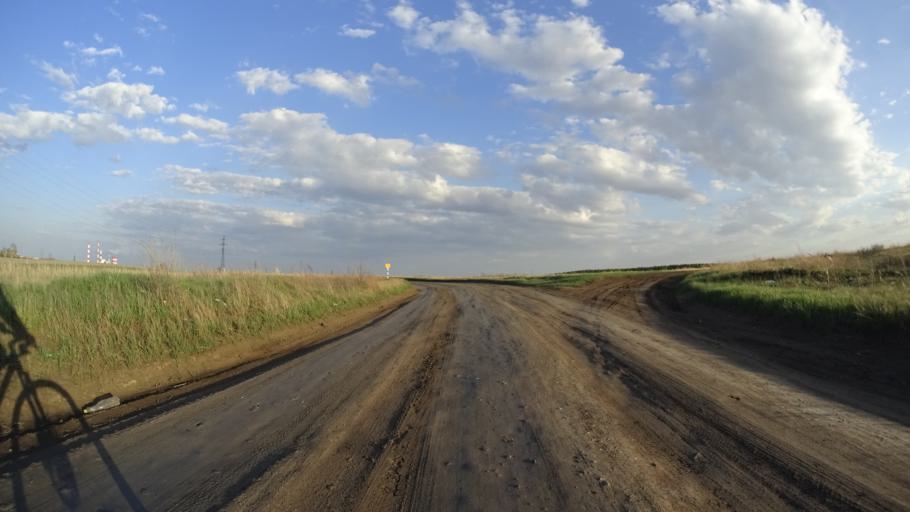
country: RU
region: Chelyabinsk
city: Troitsk
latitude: 54.0525
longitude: 61.5915
